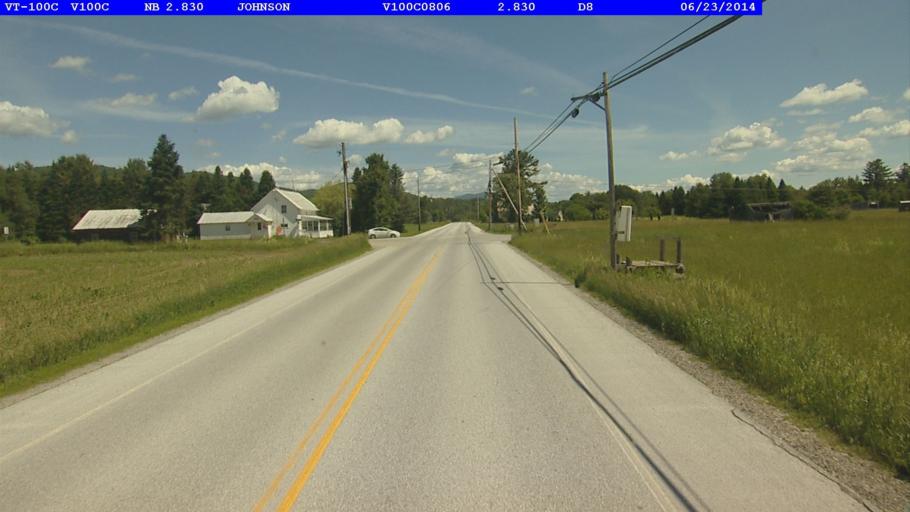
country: US
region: Vermont
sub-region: Lamoille County
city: Johnson
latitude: 44.6534
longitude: -72.6321
